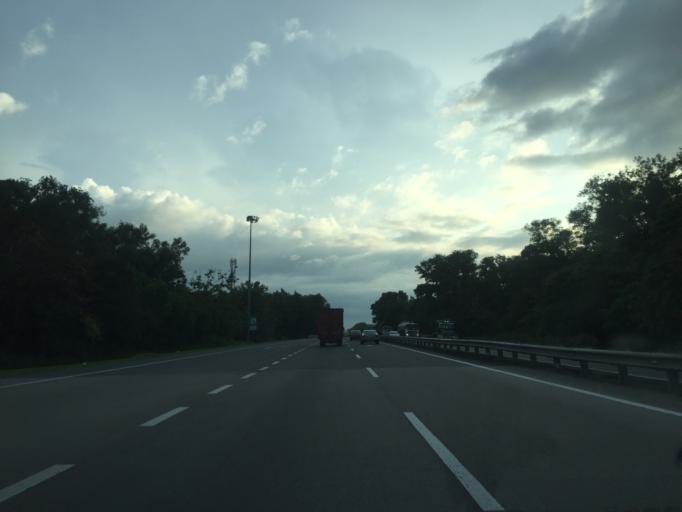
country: MY
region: Kedah
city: Sungai Petani
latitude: 5.6711
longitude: 100.5147
